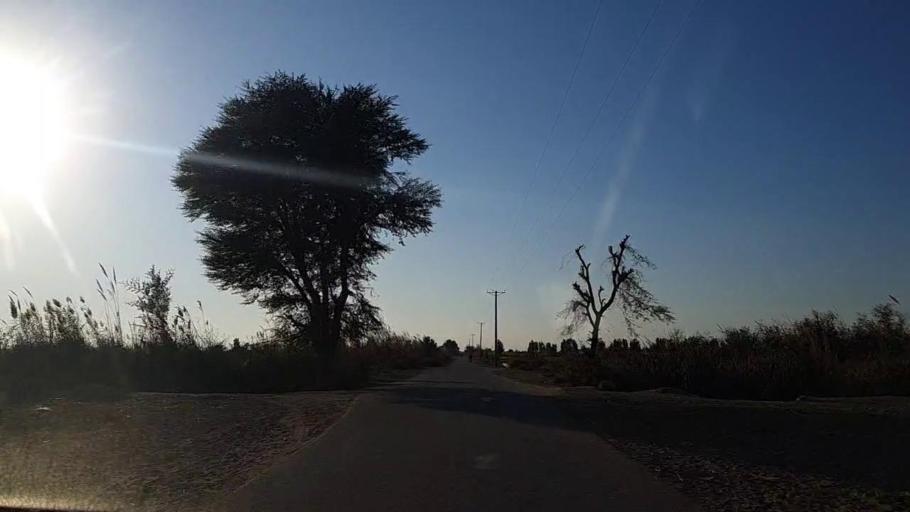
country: PK
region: Sindh
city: Khadro
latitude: 26.2790
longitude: 68.8951
